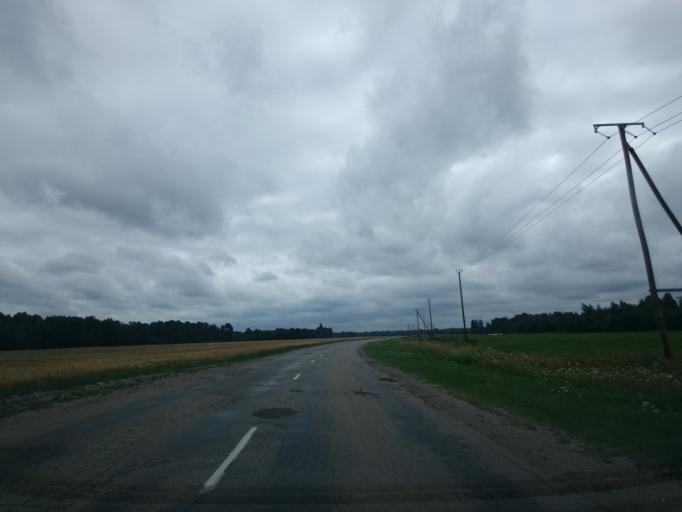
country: LV
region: Pavilostas
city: Pavilosta
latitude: 56.8282
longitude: 21.2252
